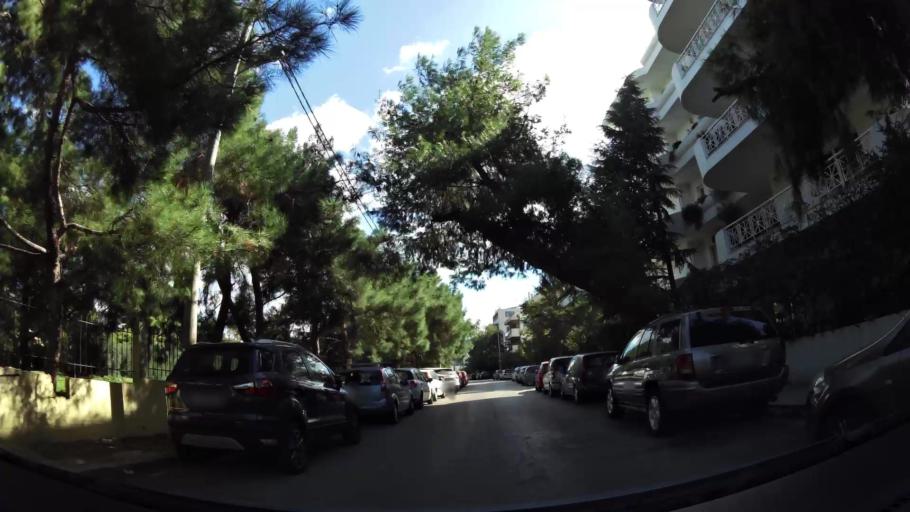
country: GR
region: Attica
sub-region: Nomarchia Athinas
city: Neo Psychiko
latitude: 38.0106
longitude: 23.7847
